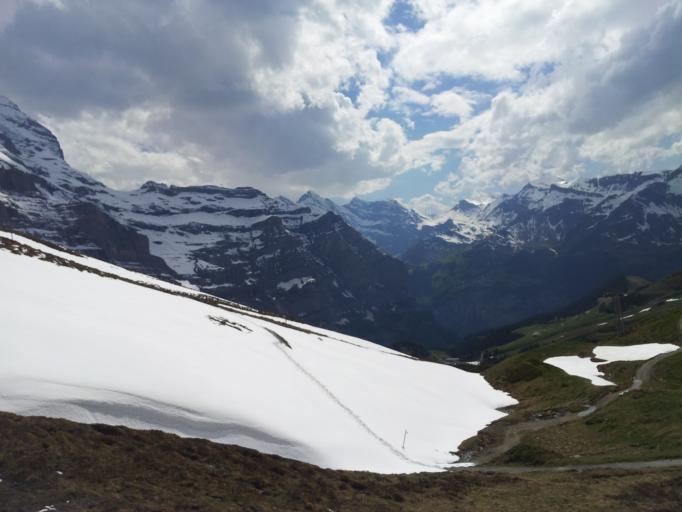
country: CH
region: Bern
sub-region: Interlaken-Oberhasli District
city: Lauterbrunnen
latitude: 46.5781
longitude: 7.9689
